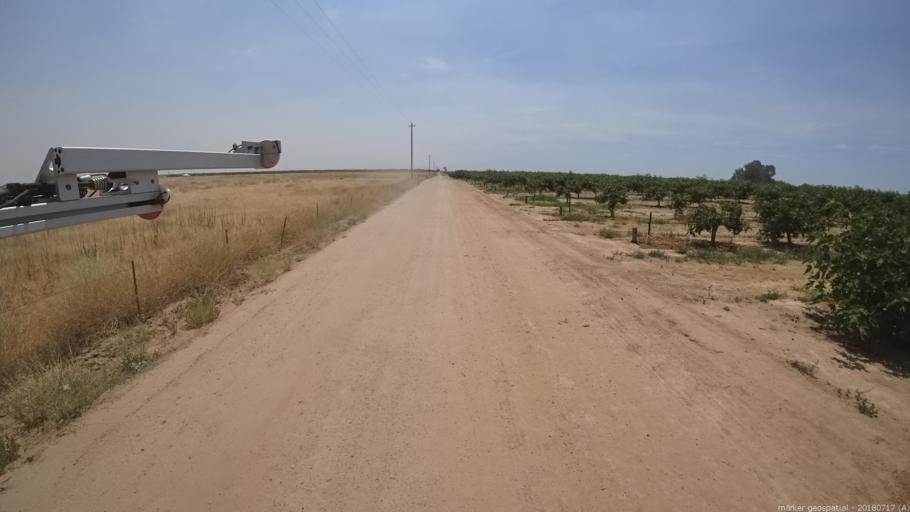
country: US
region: California
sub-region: Madera County
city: Madera Acres
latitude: 37.1263
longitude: -120.0928
